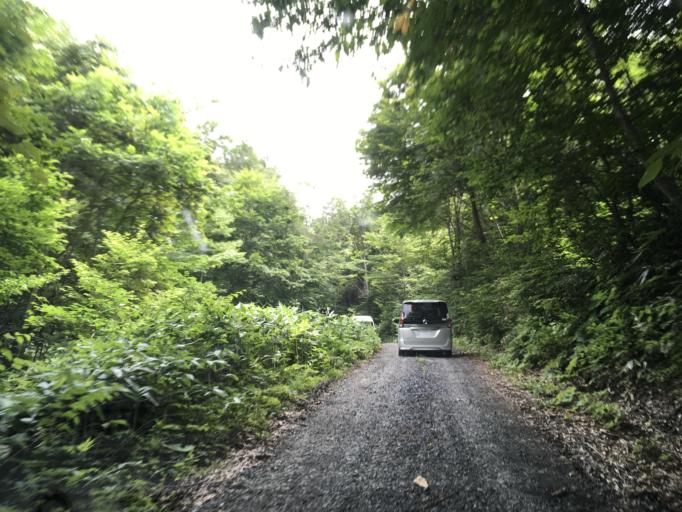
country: JP
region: Iwate
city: Ichinoseki
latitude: 38.9476
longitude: 140.8608
